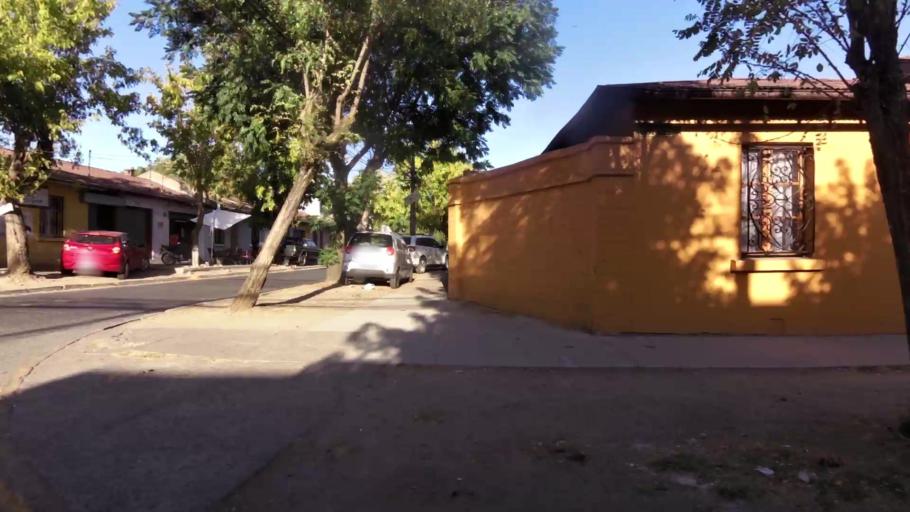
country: CL
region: Maule
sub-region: Provincia de Talca
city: Talca
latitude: -35.4245
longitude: -71.6541
